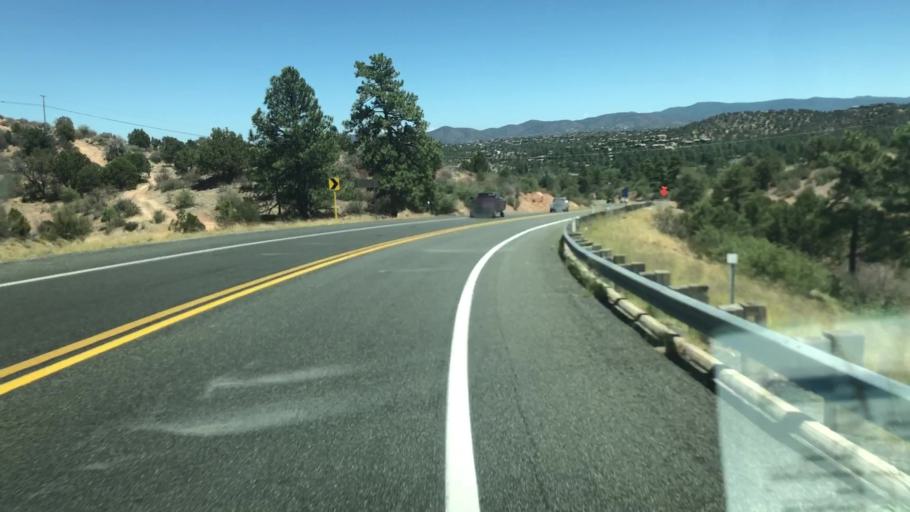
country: US
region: Arizona
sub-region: Yavapai County
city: Prescott
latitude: 34.5809
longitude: -112.5322
